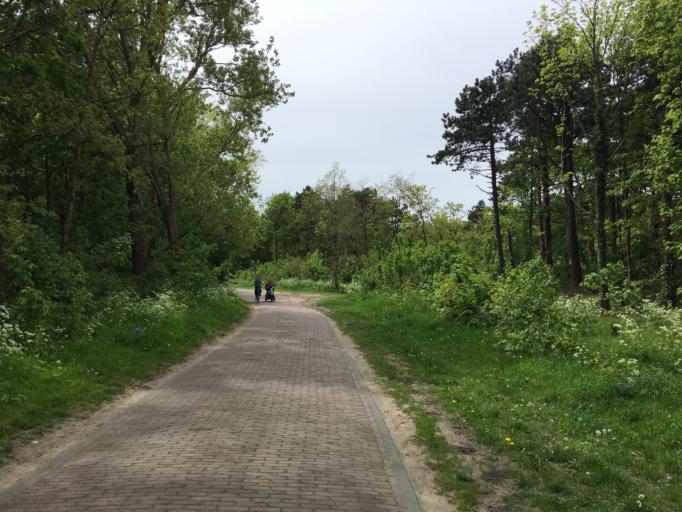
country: NL
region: North Holland
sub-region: Gemeente Bergen
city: Egmond aan Zee
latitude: 52.6178
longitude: 4.6402
